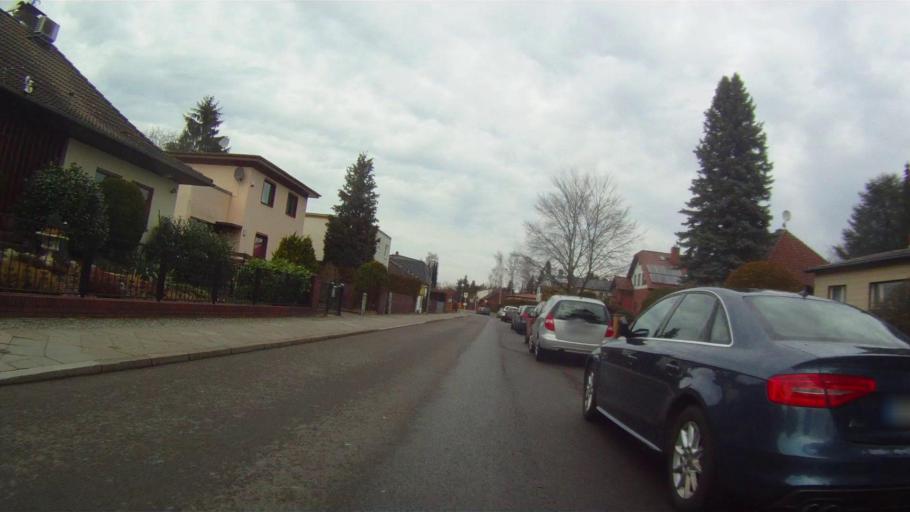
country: DE
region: Berlin
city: Lichtenrade
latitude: 52.3965
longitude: 13.3857
